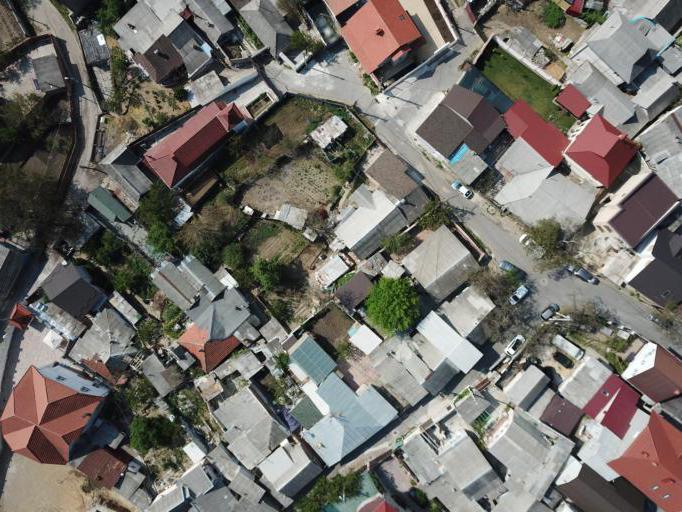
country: MD
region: Chisinau
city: Chisinau
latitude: 47.0116
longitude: 28.8493
